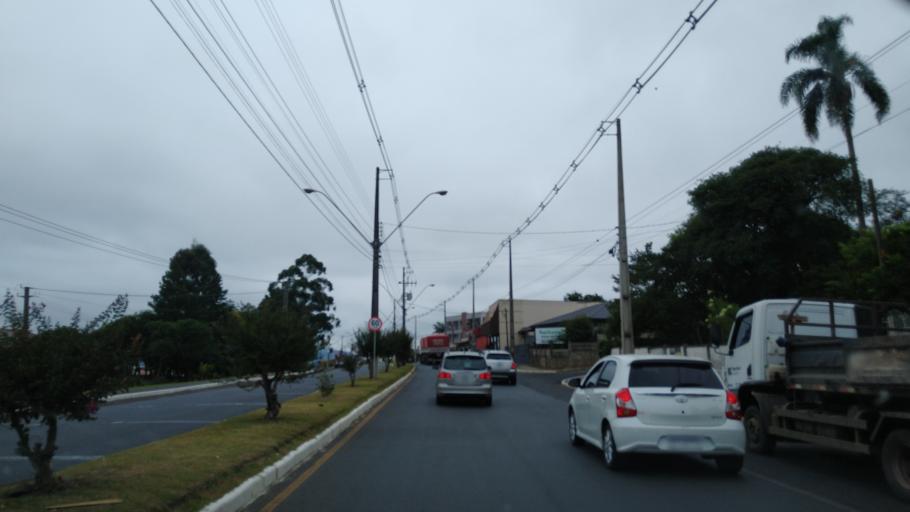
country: BR
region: Santa Catarina
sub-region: Porto Uniao
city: Porto Uniao
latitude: -26.2526
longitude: -51.0806
